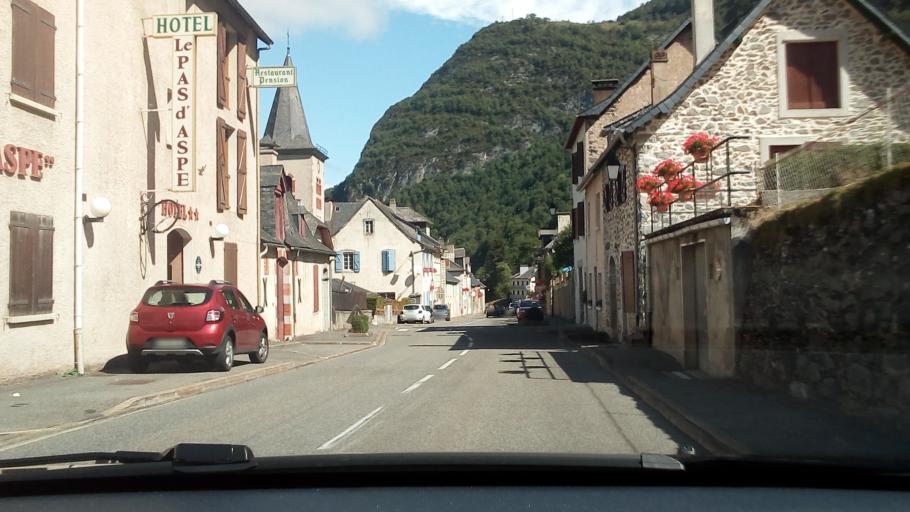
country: ES
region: Aragon
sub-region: Provincia de Huesca
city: Canfranc
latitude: 42.8713
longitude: -0.5543
